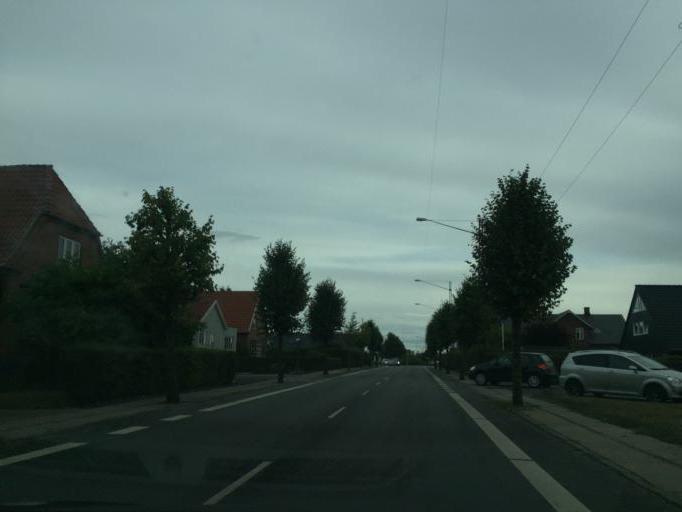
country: DK
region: South Denmark
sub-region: Middelfart Kommune
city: Middelfart
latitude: 55.5030
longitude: 9.7539
